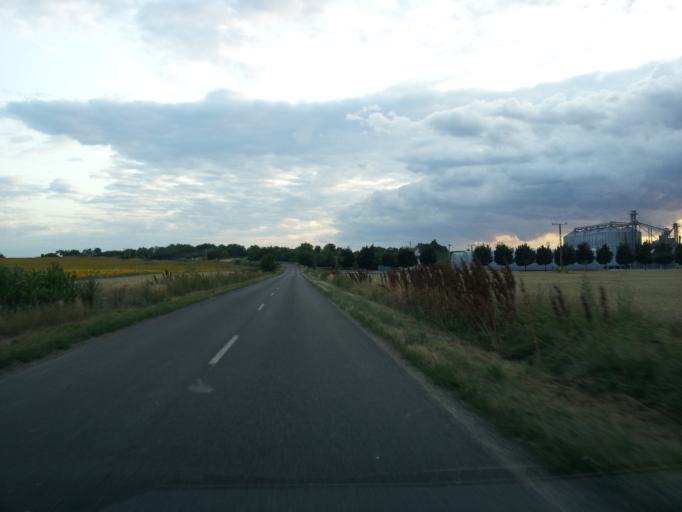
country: HU
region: Somogy
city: Adand
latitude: 46.8056
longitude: 18.1726
